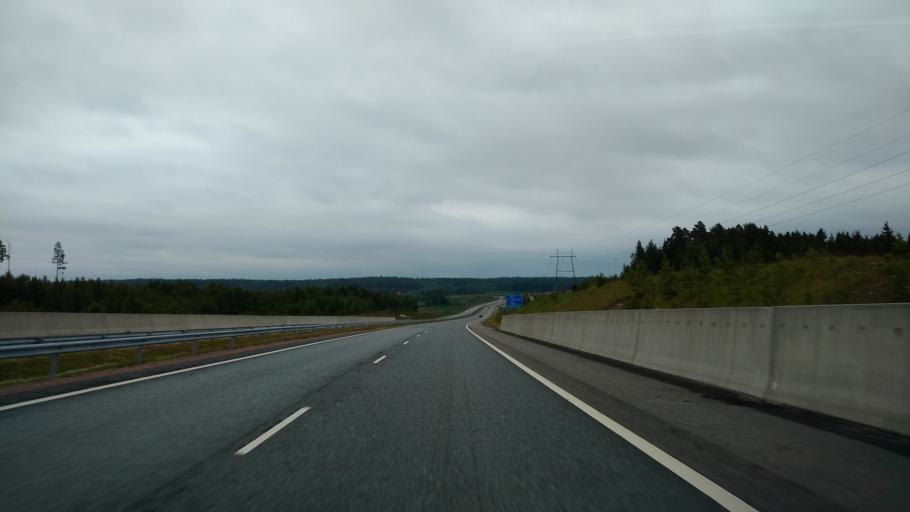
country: FI
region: Varsinais-Suomi
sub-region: Salo
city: Kiikala
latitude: 60.3919
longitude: 23.5598
